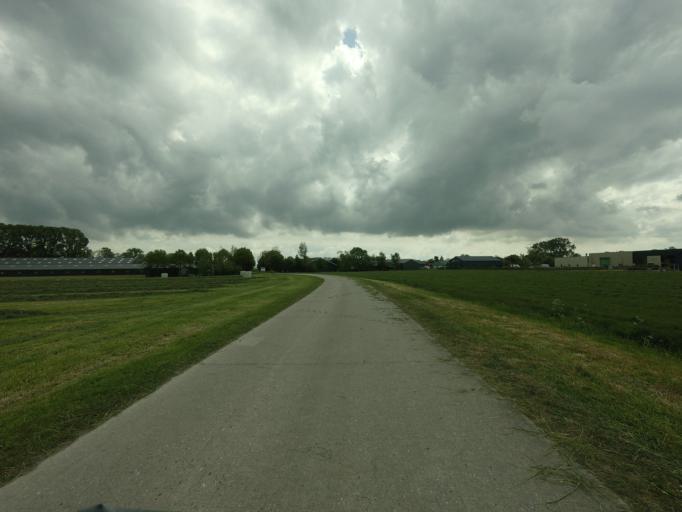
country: NL
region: Friesland
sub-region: Gemeente Littenseradiel
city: Wommels
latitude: 53.1044
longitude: 5.6228
